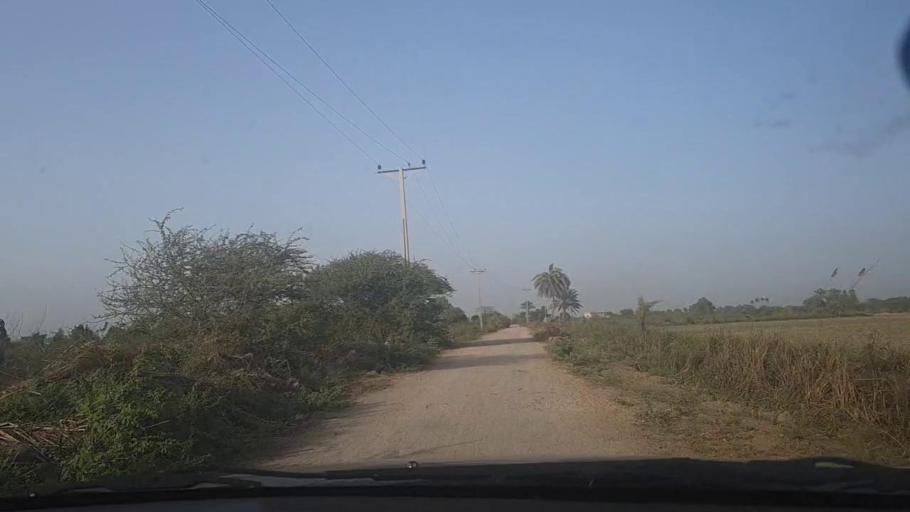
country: PK
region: Sindh
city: Keti Bandar
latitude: 24.2882
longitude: 67.6059
